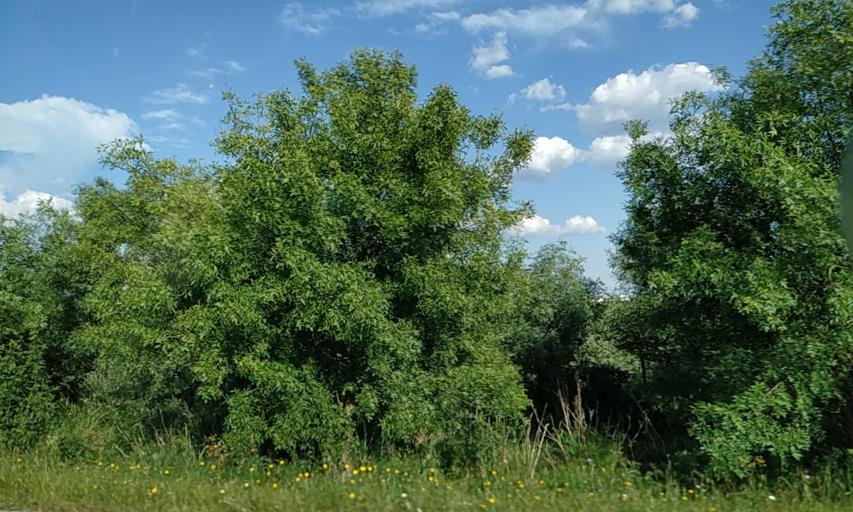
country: PT
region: Evora
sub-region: Estremoz
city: Estremoz
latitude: 38.9744
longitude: -7.4889
